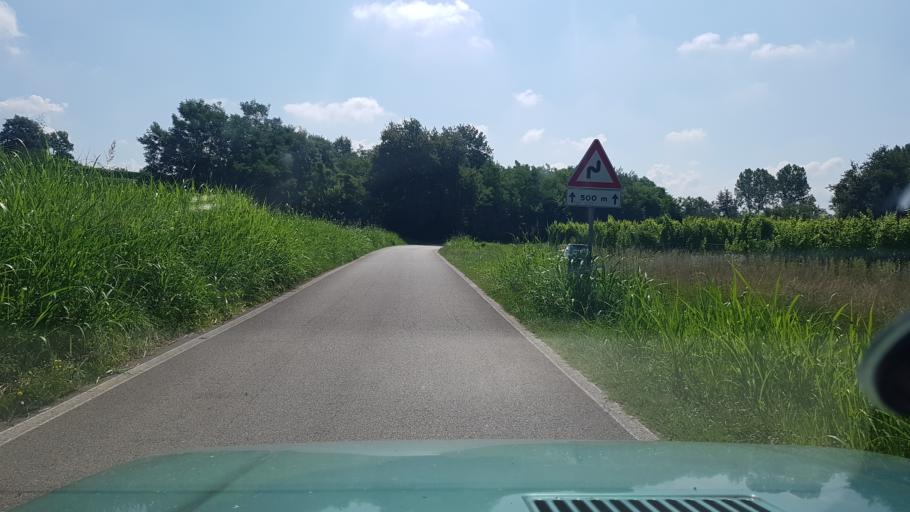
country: IT
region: Friuli Venezia Giulia
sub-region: Provincia di Gorizia
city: San Lorenzo Isontino
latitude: 45.9388
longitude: 13.5336
